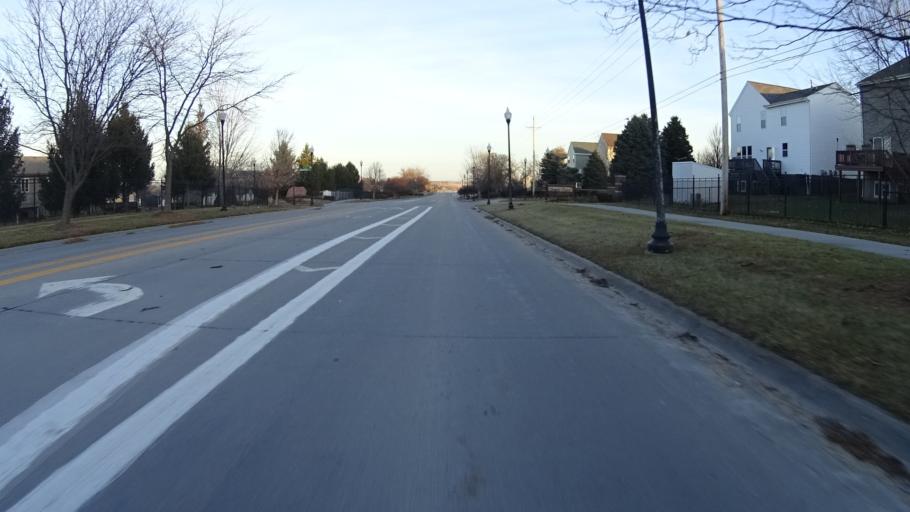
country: US
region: Nebraska
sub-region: Sarpy County
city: Papillion
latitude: 41.1326
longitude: -96.0561
